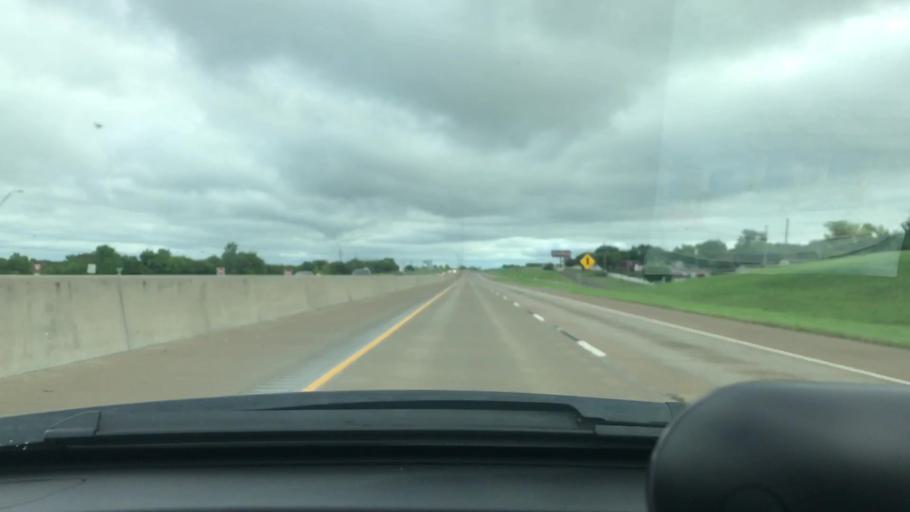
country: US
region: Texas
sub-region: Grayson County
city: Howe
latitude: 33.5111
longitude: -96.6170
